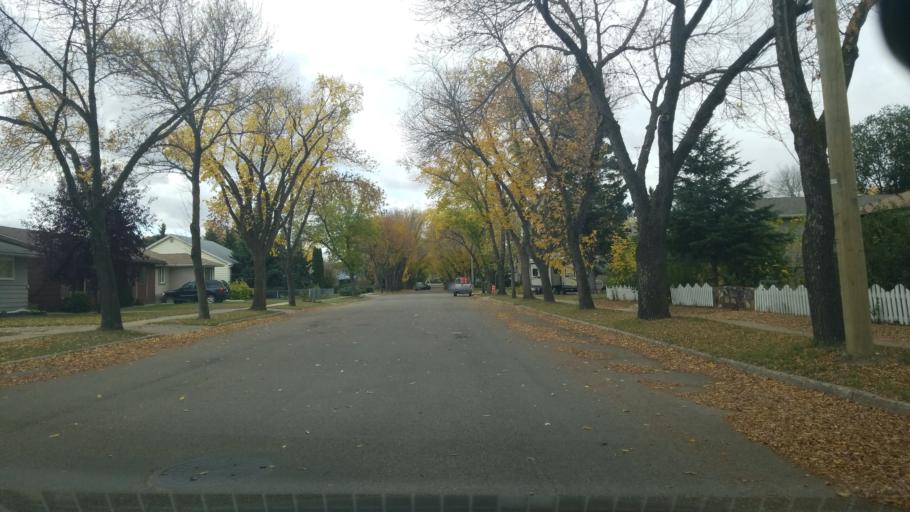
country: CA
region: Saskatchewan
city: Lloydminster
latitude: 53.2798
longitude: -110.0117
